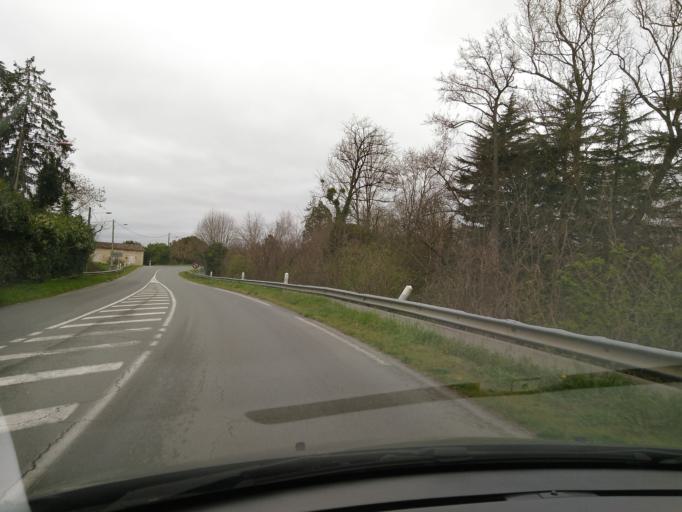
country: FR
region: Aquitaine
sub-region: Departement de la Dordogne
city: Bergerac
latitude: 44.8366
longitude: 0.4927
